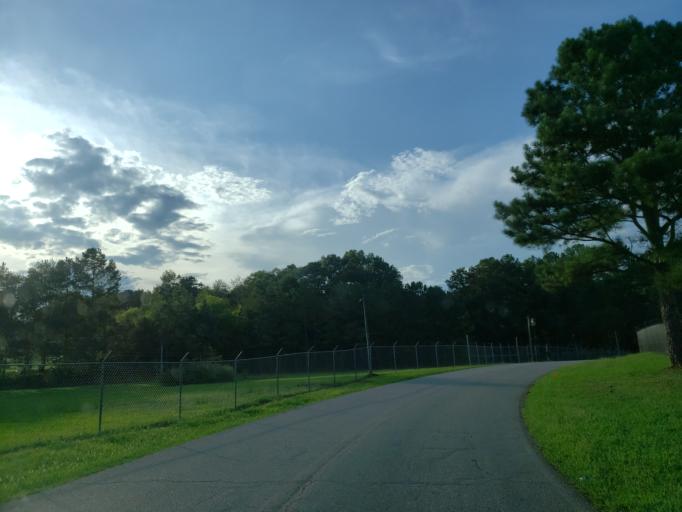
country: US
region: Georgia
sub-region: Bartow County
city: Euharlee
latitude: 34.2360
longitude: -84.9543
